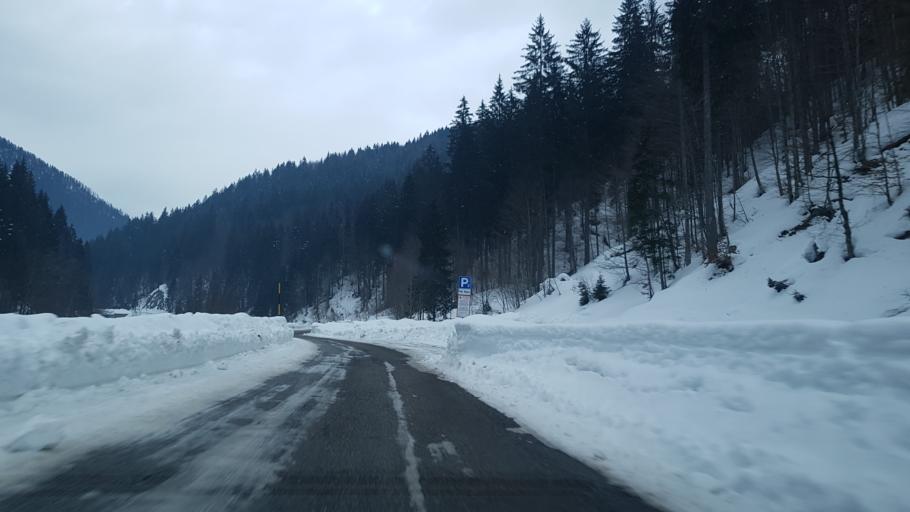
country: IT
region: Friuli Venezia Giulia
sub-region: Provincia di Udine
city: Malborghetto
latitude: 46.5347
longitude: 13.4723
